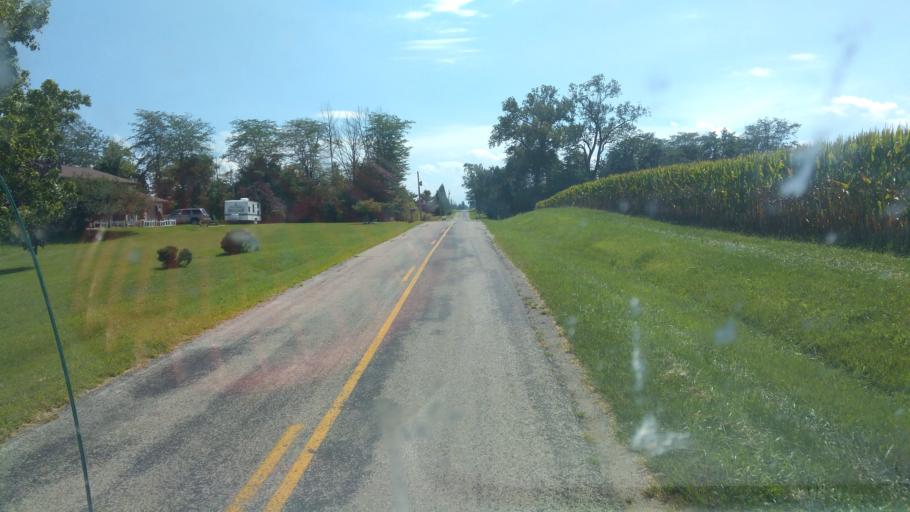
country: US
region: Ohio
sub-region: Wyandot County
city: Upper Sandusky
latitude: 40.6506
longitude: -83.3430
